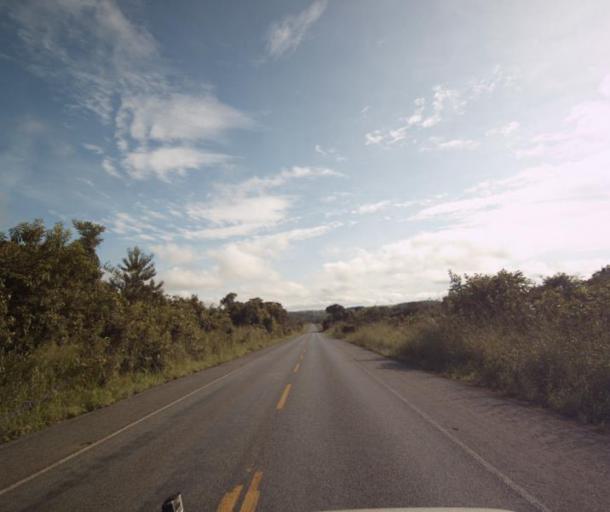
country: BR
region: Goias
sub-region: Padre Bernardo
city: Padre Bernardo
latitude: -15.5018
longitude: -48.6205
